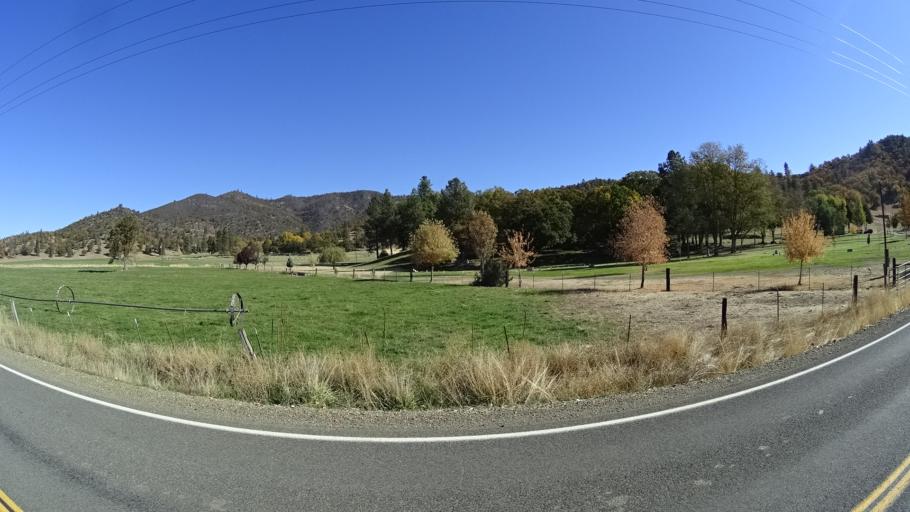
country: US
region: California
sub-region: Siskiyou County
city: Yreka
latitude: 41.5898
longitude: -122.8370
